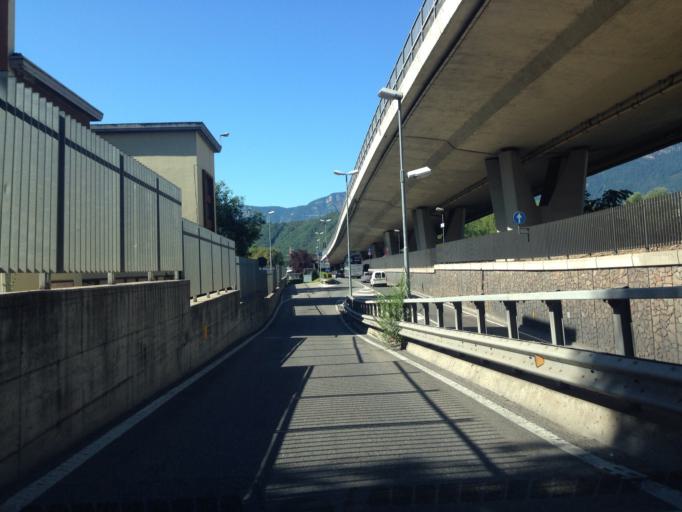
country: IT
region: Trentino-Alto Adige
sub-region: Bolzano
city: Bolzano
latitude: 46.4808
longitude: 11.3233
